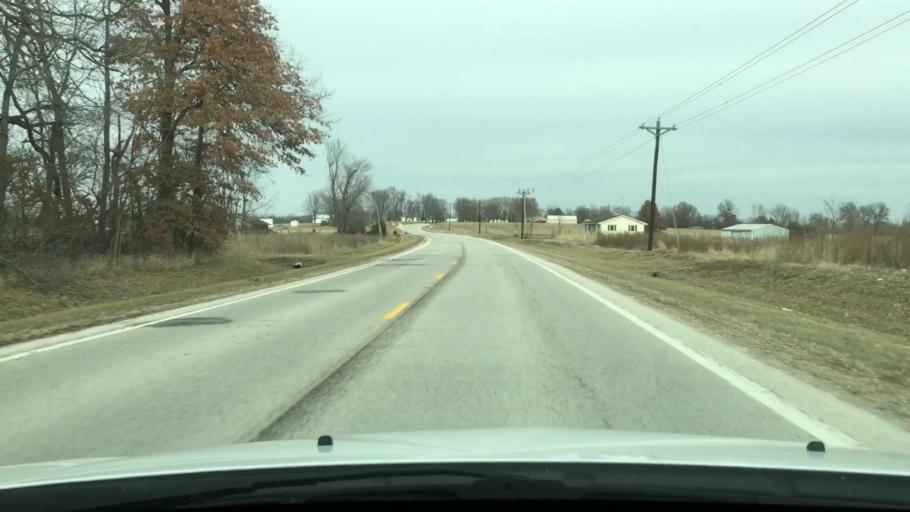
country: US
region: Illinois
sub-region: Pike County
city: Pittsfield
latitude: 39.5683
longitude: -90.9143
